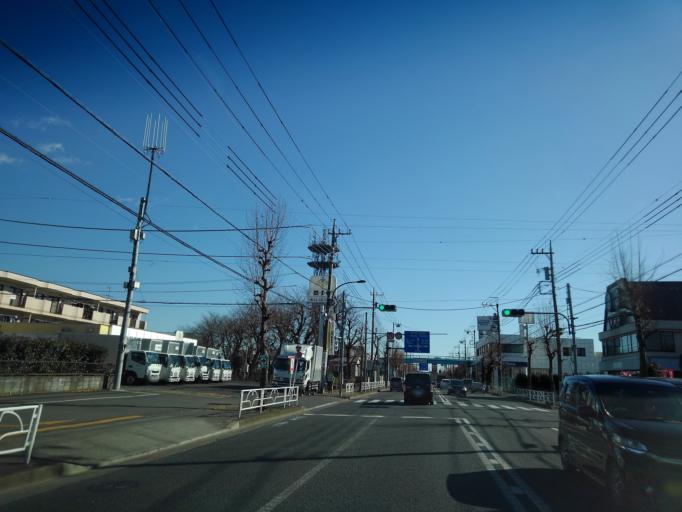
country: JP
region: Tokyo
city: Fussa
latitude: 35.7561
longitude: 139.3724
